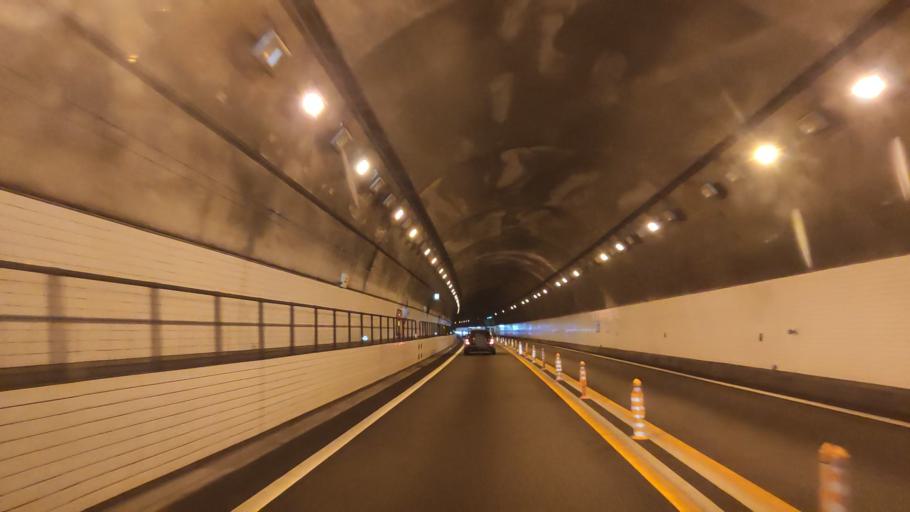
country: JP
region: Tokushima
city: Ikedacho
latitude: 34.0254
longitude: 133.7811
